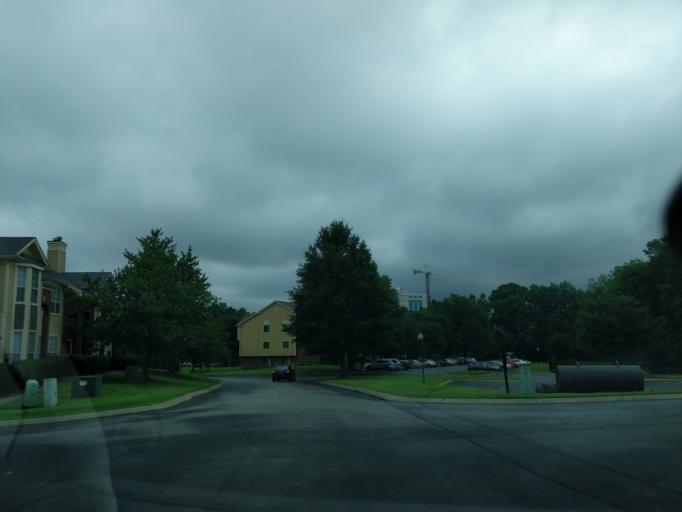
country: US
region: Tennessee
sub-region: Davidson County
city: Lakewood
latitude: 36.1718
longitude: -86.6100
